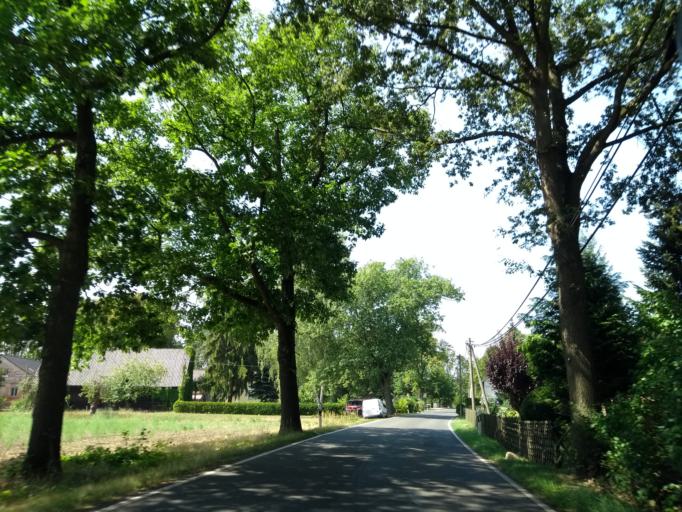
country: DE
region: Brandenburg
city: Burg
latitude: 51.8429
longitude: 14.1465
